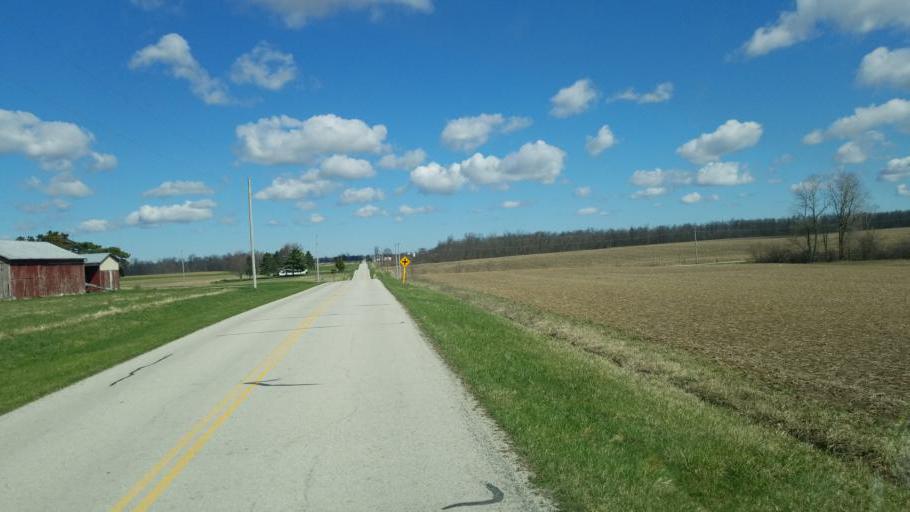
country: US
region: Ohio
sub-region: Sandusky County
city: Mount Carmel
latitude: 41.1451
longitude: -82.9382
